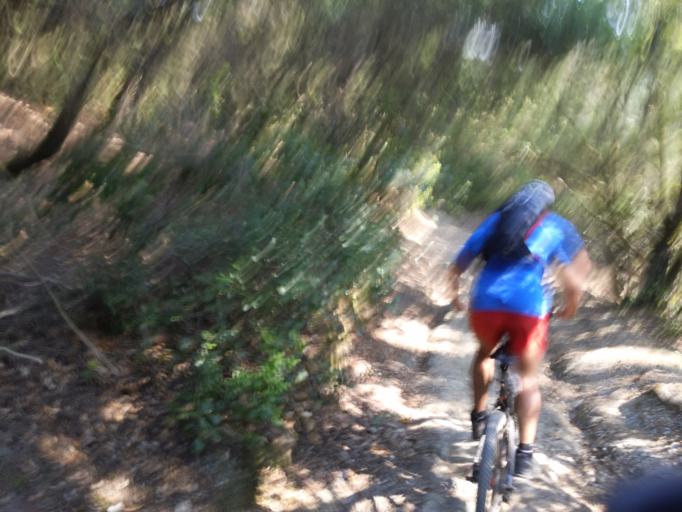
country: ES
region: Catalonia
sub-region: Provincia de Barcelona
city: Cerdanyola del Valles
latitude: 41.4682
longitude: 2.1312
